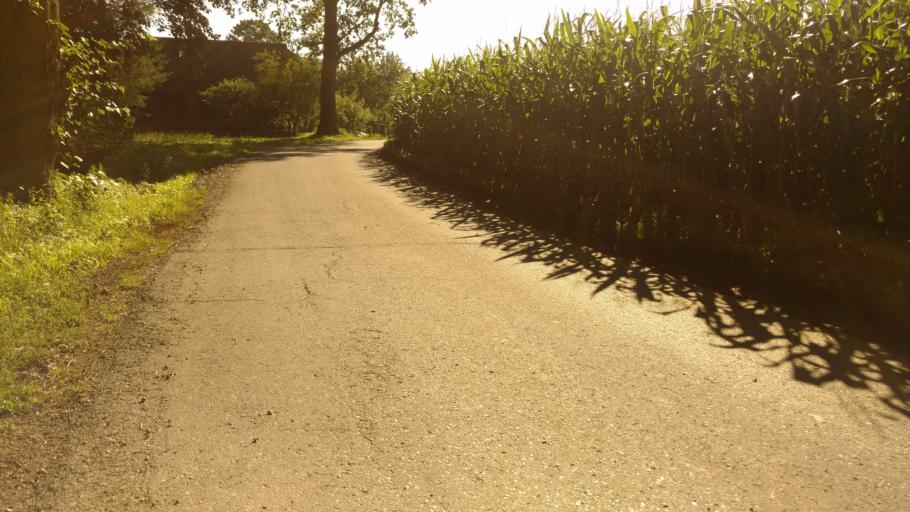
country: PL
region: Silesian Voivodeship
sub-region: Powiat pszczynski
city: Jankowice
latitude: 49.9890
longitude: 19.0055
